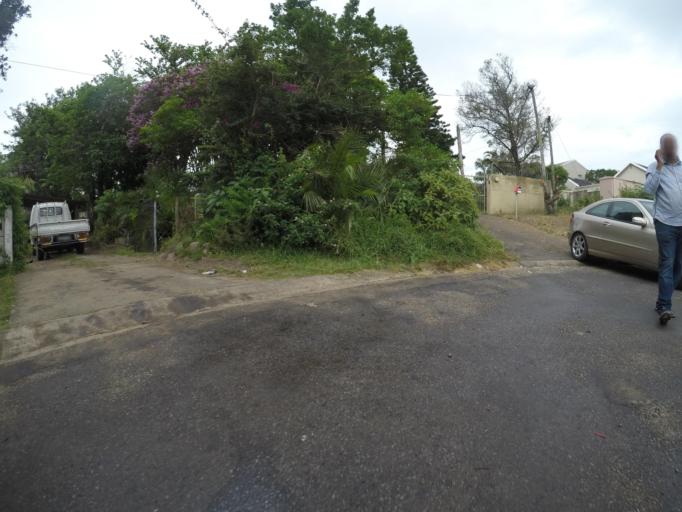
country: ZA
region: Eastern Cape
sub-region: Buffalo City Metropolitan Municipality
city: East London
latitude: -32.9895
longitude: 27.8558
